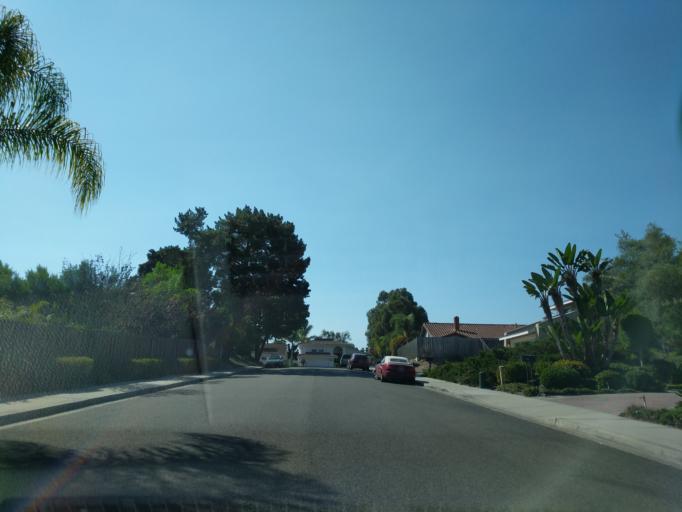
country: US
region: California
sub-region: San Diego County
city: Lake San Marcos
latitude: 33.0817
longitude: -117.2419
